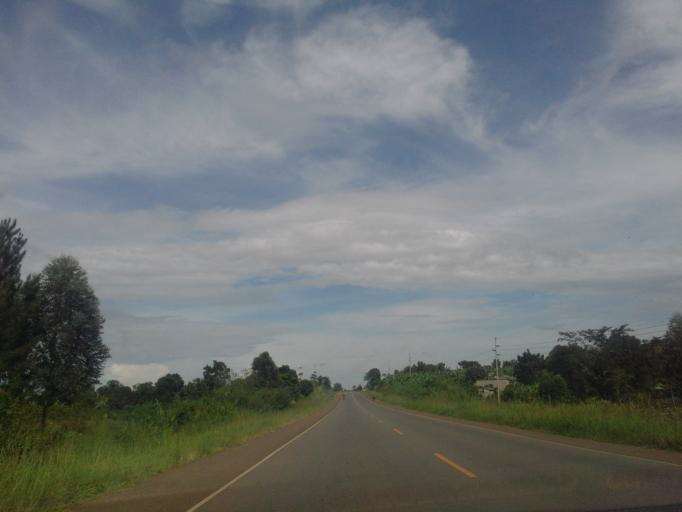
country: UG
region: Central Region
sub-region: Lwengo District
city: Lwengo
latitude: -0.3701
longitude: 31.5296
